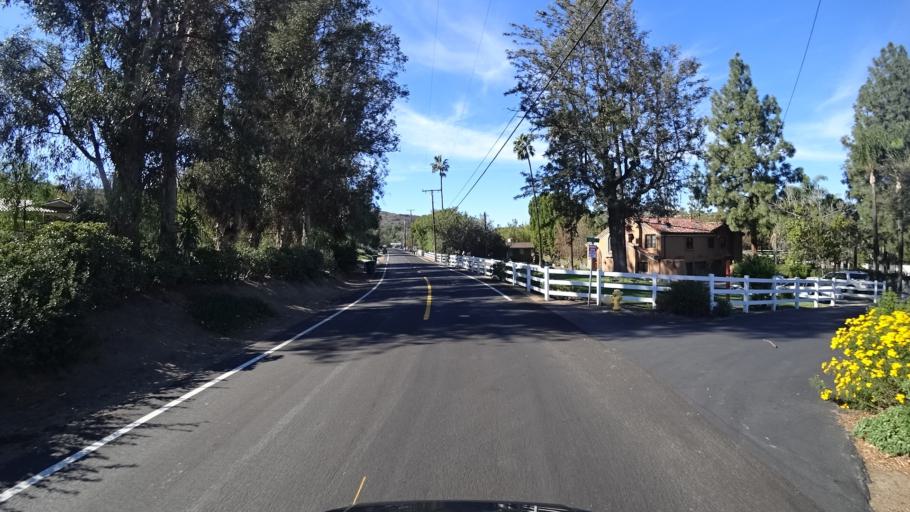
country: US
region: California
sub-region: Orange County
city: Villa Park
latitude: 33.8008
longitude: -117.7846
